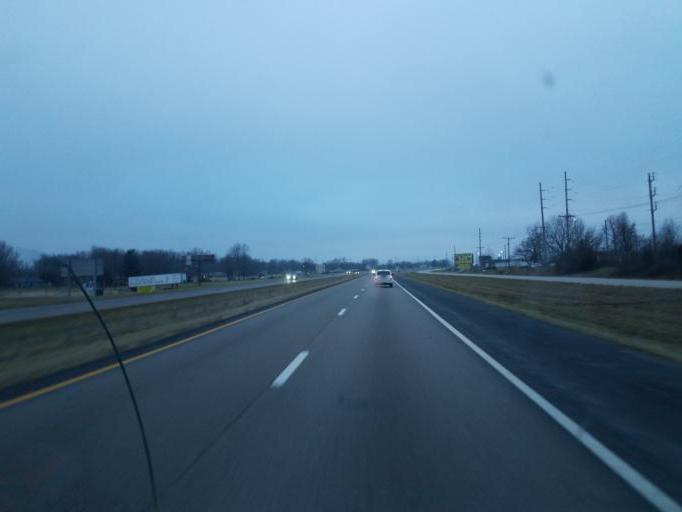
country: US
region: Missouri
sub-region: Phelps County
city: Saint James
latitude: 37.9967
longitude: -91.6315
